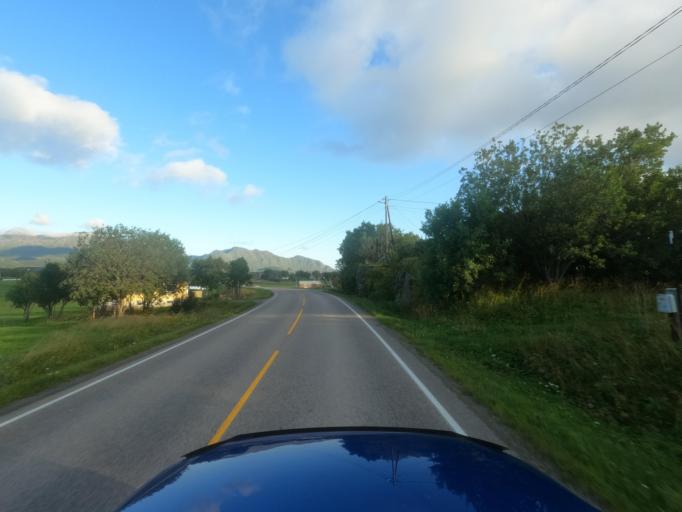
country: NO
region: Nordland
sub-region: Vestvagoy
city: Gravdal
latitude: 68.1377
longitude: 13.5557
